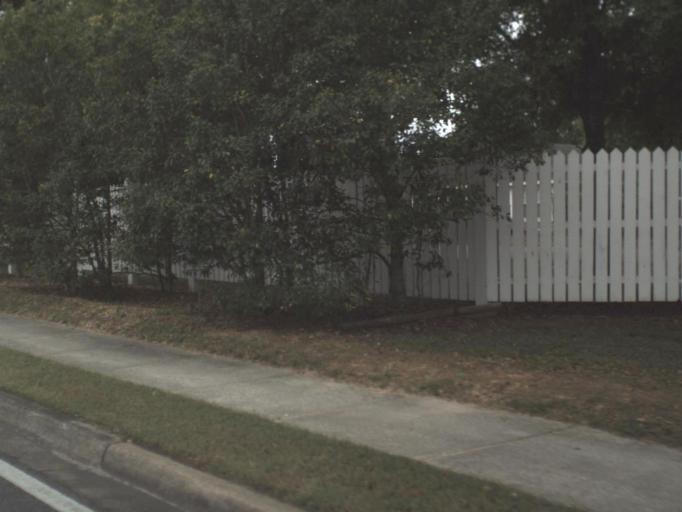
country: US
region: Florida
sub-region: Escambia County
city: Bellview
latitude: 30.4607
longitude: -87.2826
